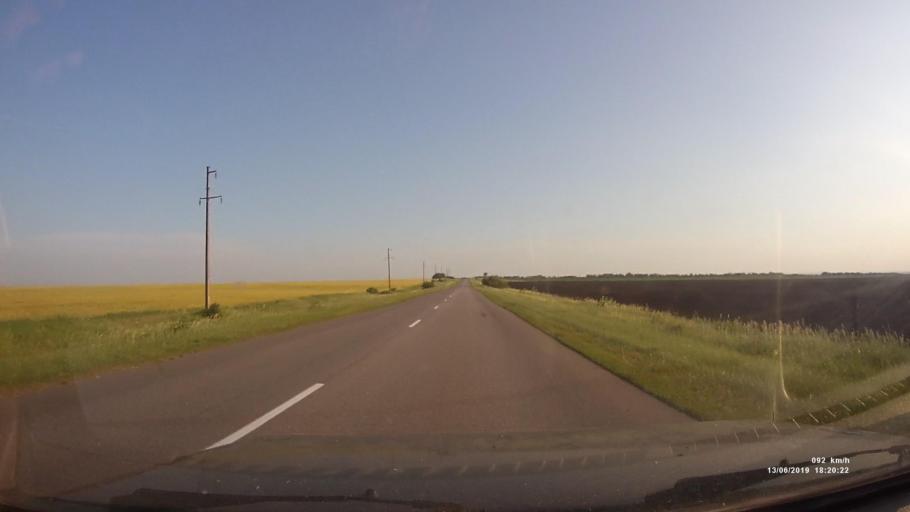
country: RU
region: Rostov
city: Kazanskaya
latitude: 49.8848
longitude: 41.2996
